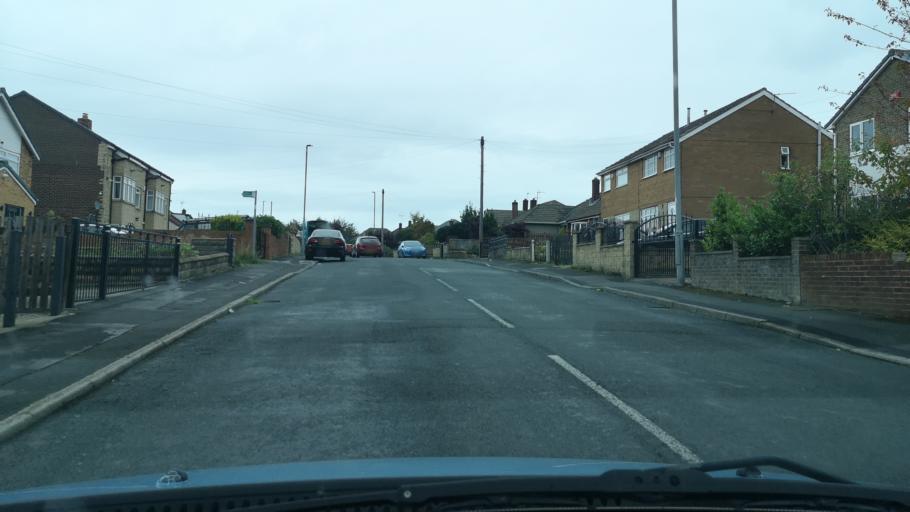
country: GB
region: England
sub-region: Kirklees
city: Heckmondwike
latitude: 53.7183
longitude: -1.6711
